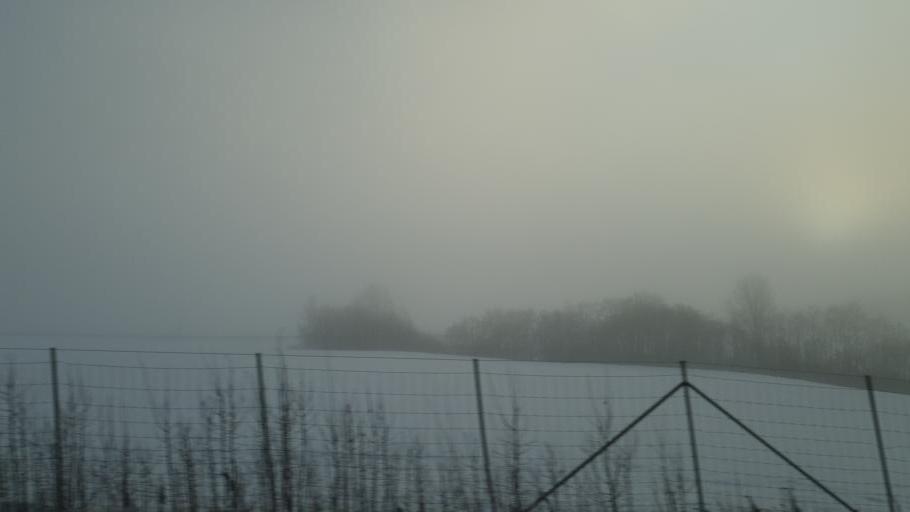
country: NO
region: Akershus
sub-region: Sorum
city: Frogner
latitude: 60.0129
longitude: 11.1089
